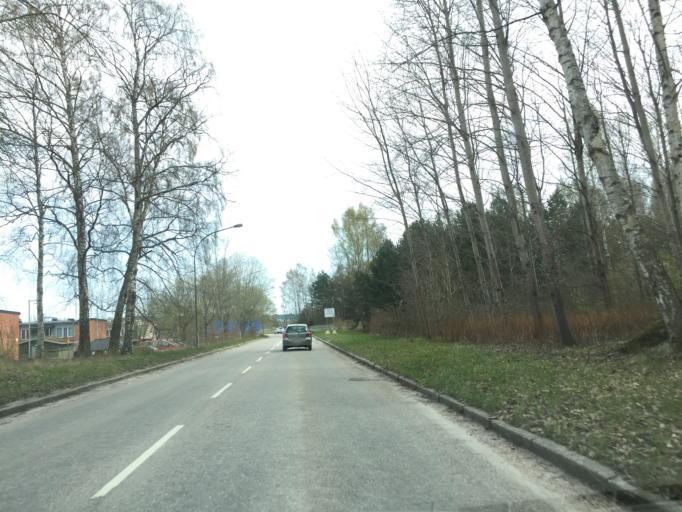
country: SE
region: OErebro
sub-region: Orebro Kommun
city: Orebro
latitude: 59.2943
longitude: 15.1926
